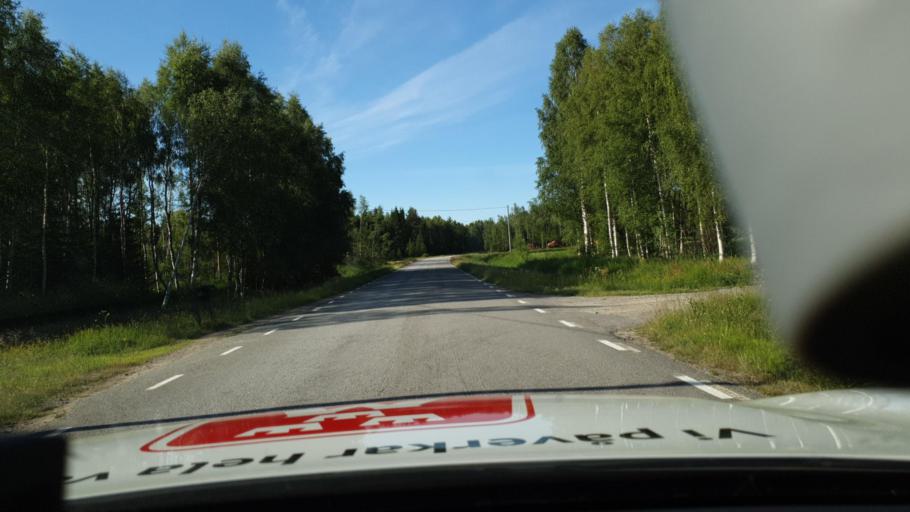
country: SE
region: Norrbotten
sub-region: Kalix Kommun
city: Toere
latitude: 65.8589
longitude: 22.6762
